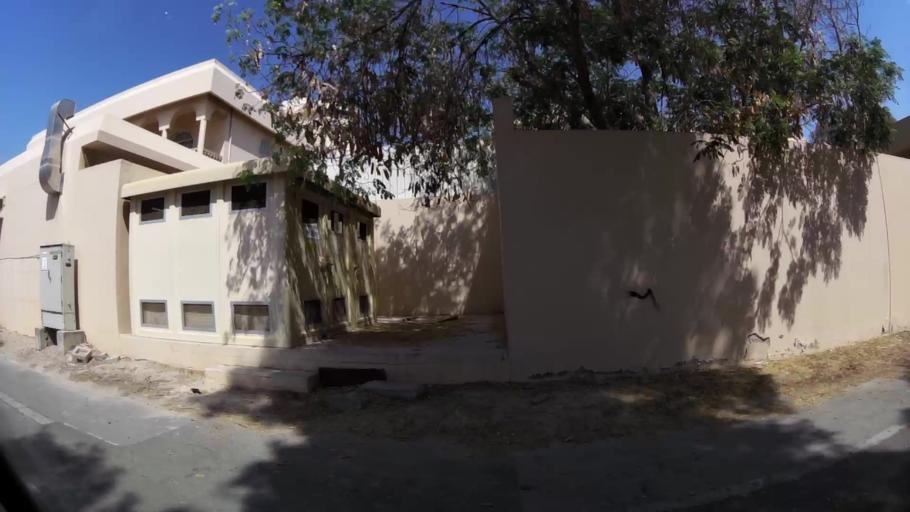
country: AE
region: Ash Shariqah
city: Sharjah
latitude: 25.2673
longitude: 55.3696
